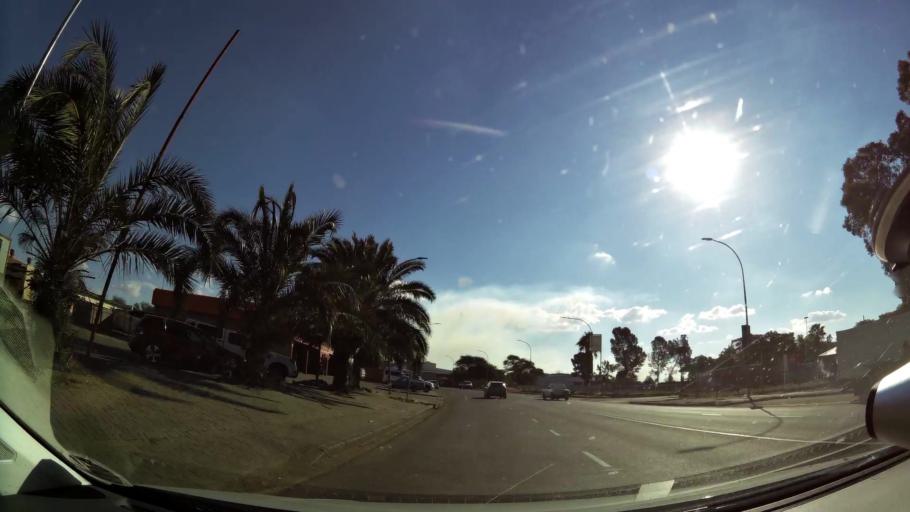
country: ZA
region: Northern Cape
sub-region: Frances Baard District Municipality
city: Kimberley
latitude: -28.7308
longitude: 24.7642
